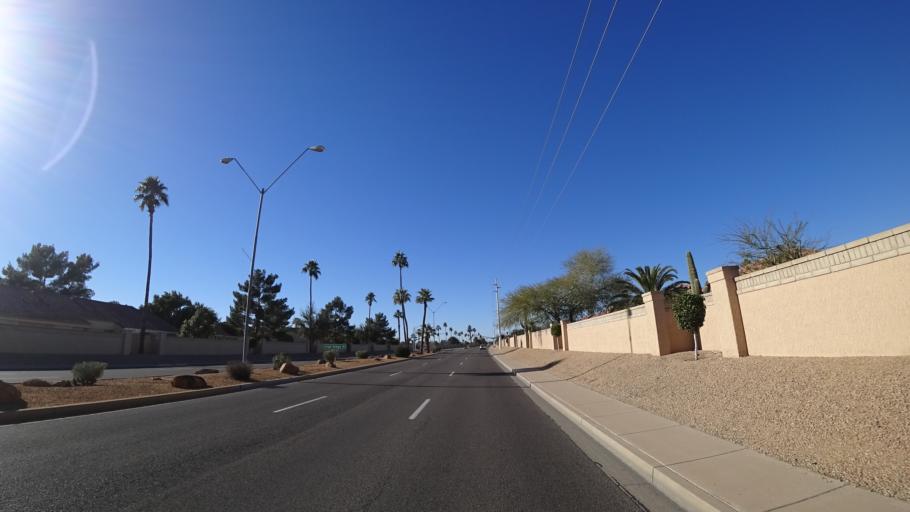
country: US
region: Arizona
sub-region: Maricopa County
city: Sun City West
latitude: 33.6649
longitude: -112.3635
